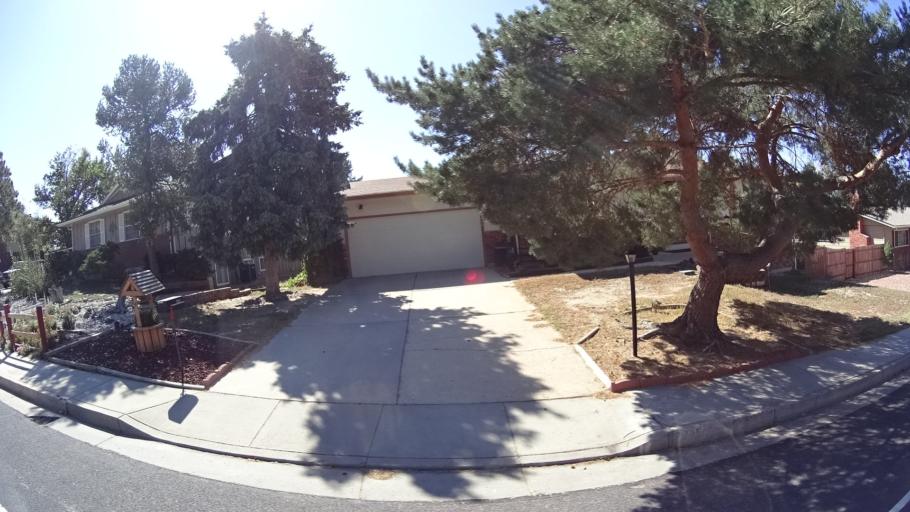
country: US
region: Colorado
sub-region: El Paso County
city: Cimarron Hills
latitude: 38.9110
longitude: -104.7676
